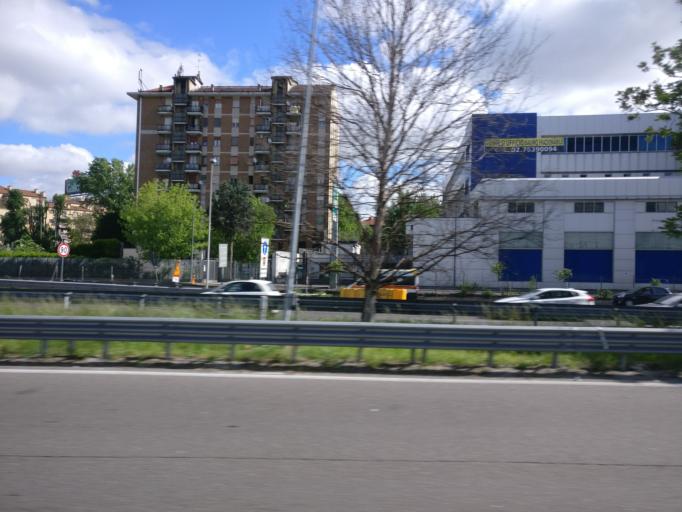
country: IT
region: Lombardy
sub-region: Citta metropolitana di Milano
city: Baranzate
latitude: 45.5130
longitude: 9.1247
